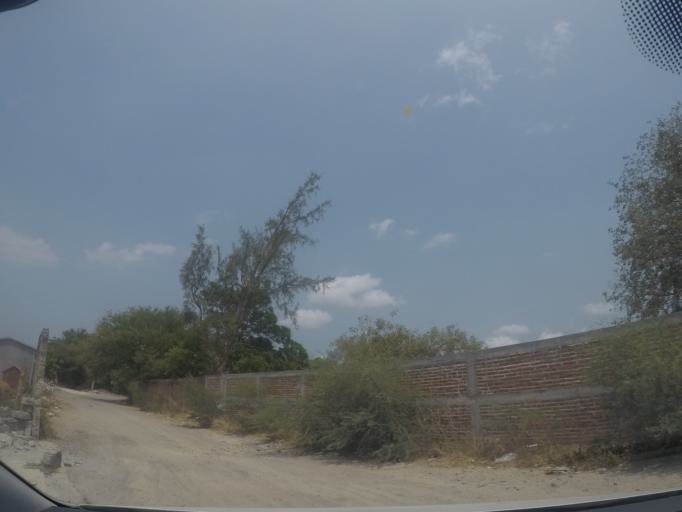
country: MX
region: Oaxaca
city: Asuncion Ixtaltepec
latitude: 16.5038
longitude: -95.0665
